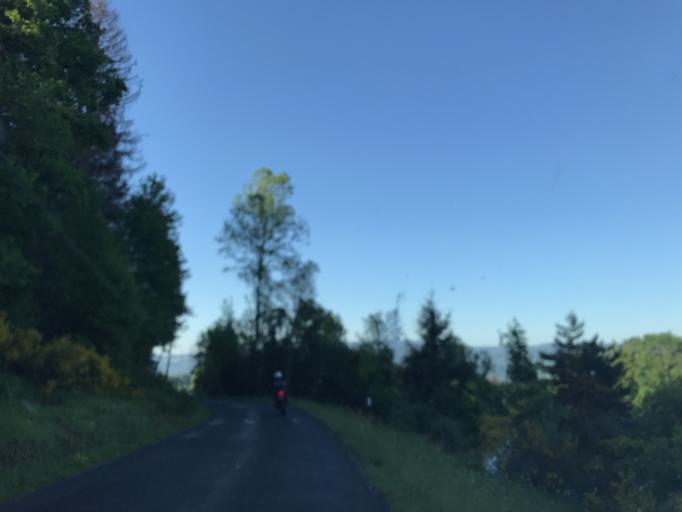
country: FR
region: Auvergne
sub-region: Departement du Puy-de-Dome
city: Job
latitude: 45.6838
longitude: 3.6967
